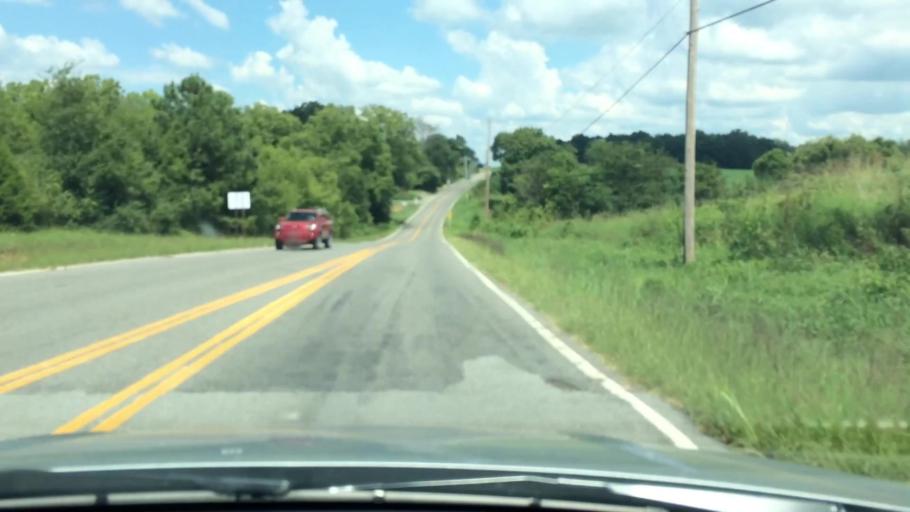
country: US
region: Tennessee
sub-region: McMinn County
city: Athens
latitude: 35.4608
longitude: -84.5643
